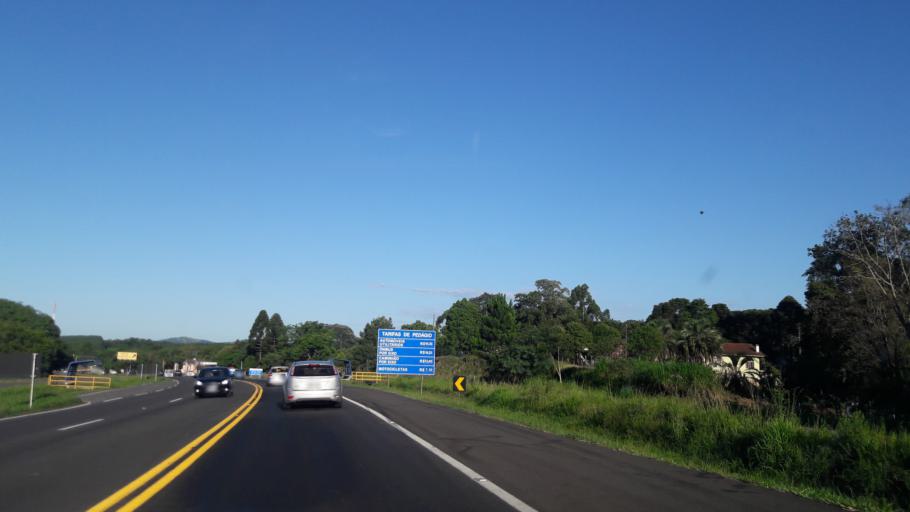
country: BR
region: Parana
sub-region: Prudentopolis
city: Prudentopolis
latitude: -25.3131
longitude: -51.1740
